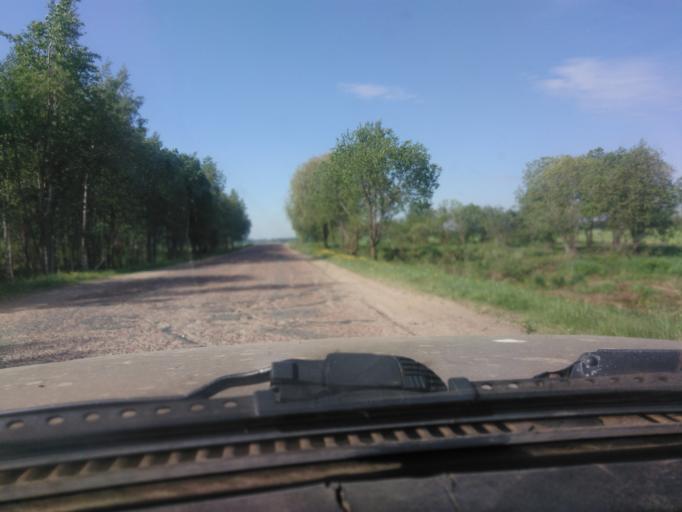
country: BY
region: Mogilev
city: Myazhysyatki
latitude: 53.7932
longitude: 30.0179
